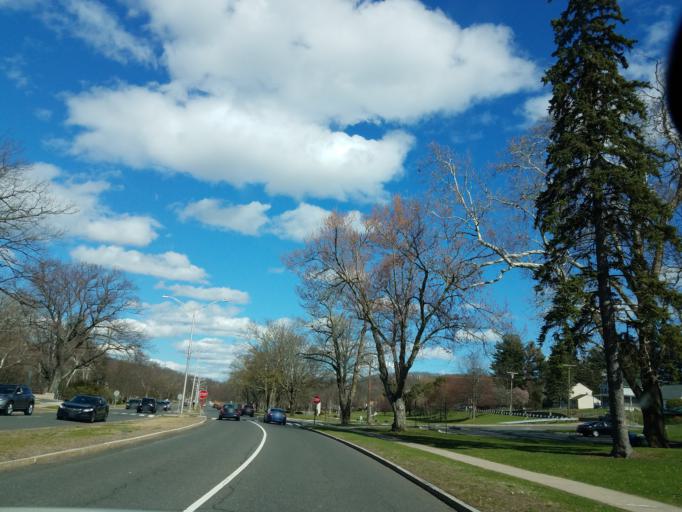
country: US
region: Connecticut
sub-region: Hartford County
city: Bristol
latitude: 41.6692
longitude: -72.9348
